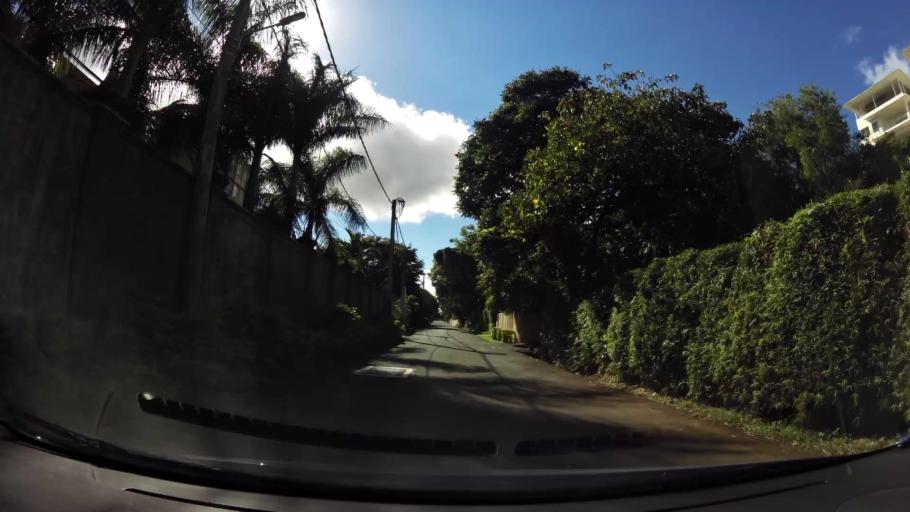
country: MU
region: Plaines Wilhems
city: Curepipe
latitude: -20.3104
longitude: 57.5081
